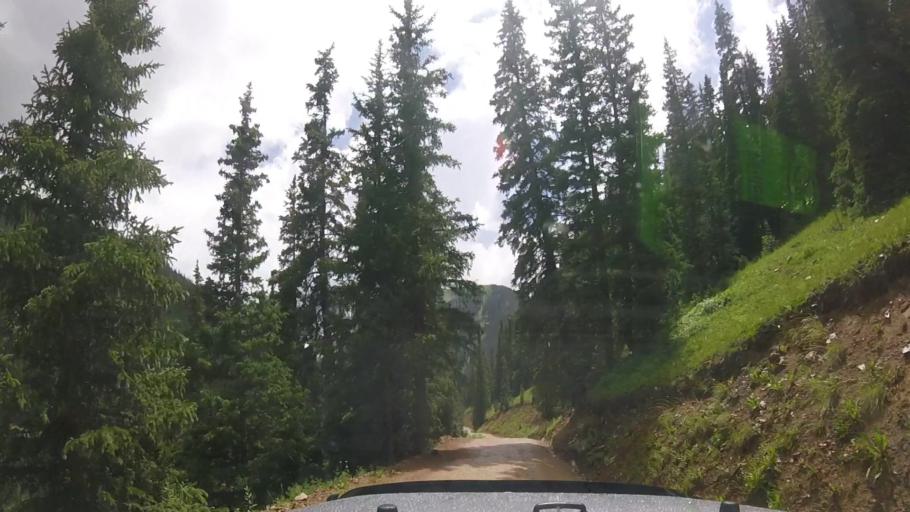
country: US
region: Colorado
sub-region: San Juan County
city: Silverton
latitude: 37.8970
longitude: -107.6471
